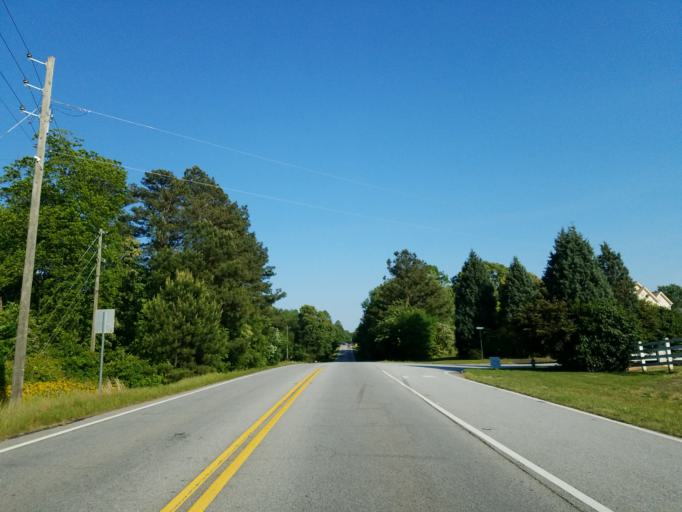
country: US
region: Georgia
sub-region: Carroll County
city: Villa Rica
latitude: 33.7626
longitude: -84.9478
